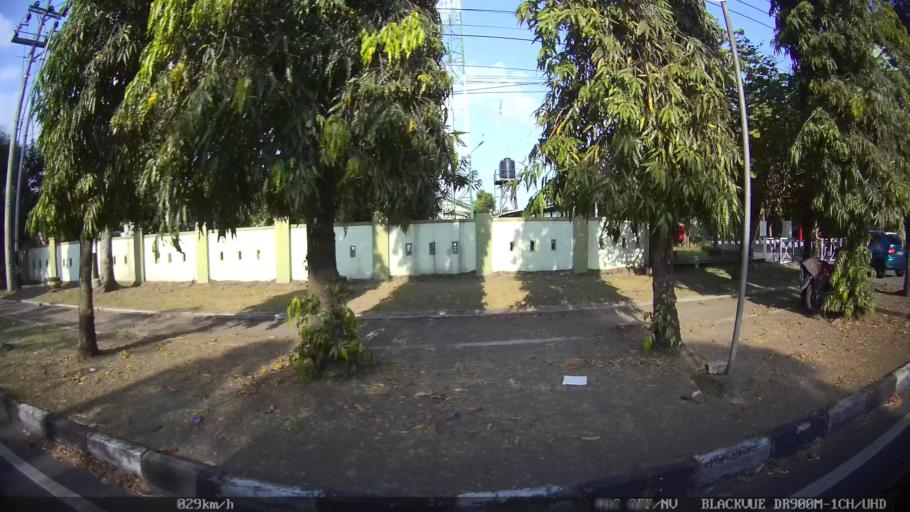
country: ID
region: Daerah Istimewa Yogyakarta
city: Gamping Lor
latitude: -7.7778
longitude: 110.3318
